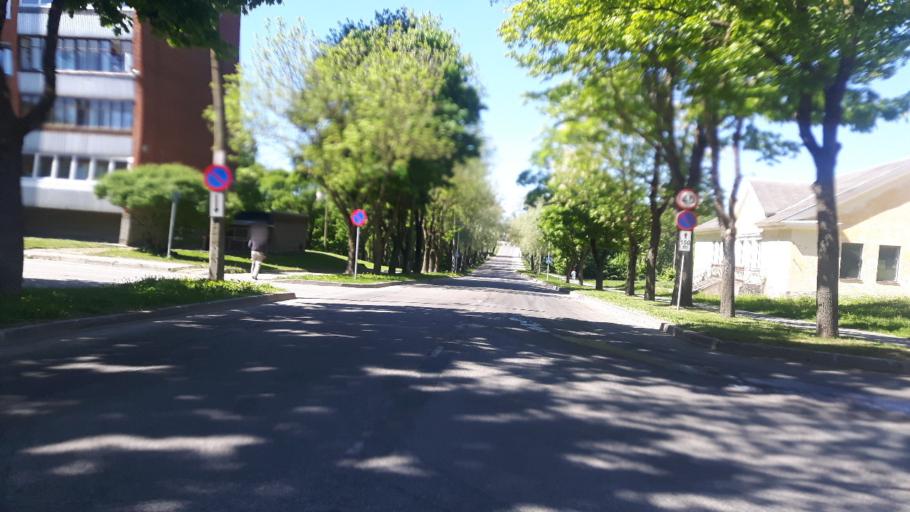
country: EE
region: Ida-Virumaa
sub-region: Sillamaee linn
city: Sillamae
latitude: 59.3980
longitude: 27.7546
